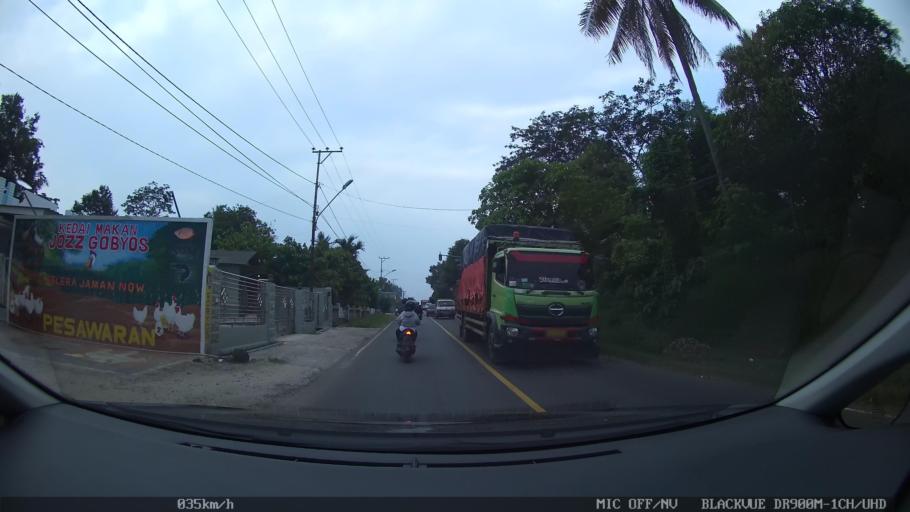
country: ID
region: Lampung
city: Gedongtataan
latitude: -5.3679
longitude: 105.1388
